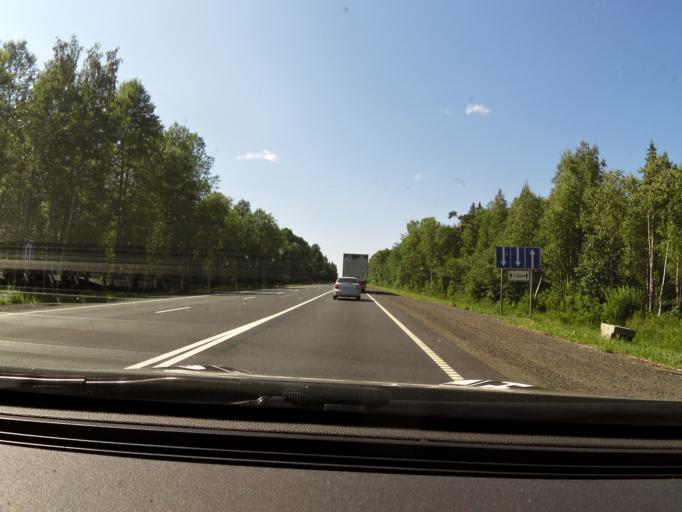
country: RU
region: Novgorod
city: Proletariy
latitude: 58.3750
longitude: 32.0297
